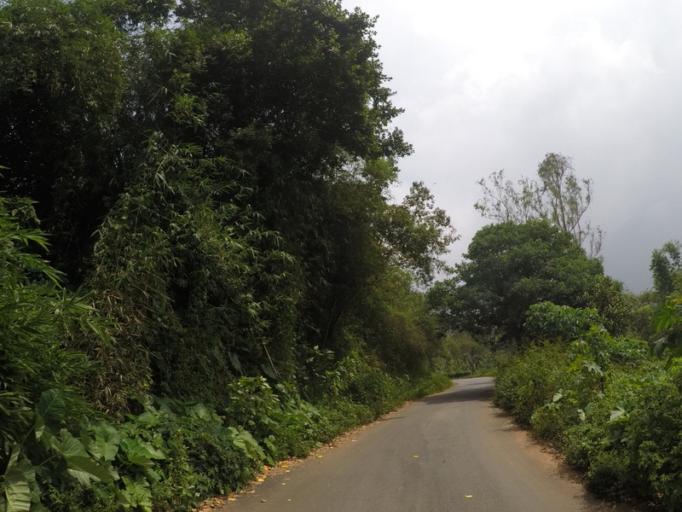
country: IN
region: Karnataka
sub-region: Chikmagalur
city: Mudigere
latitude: 13.1656
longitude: 75.4578
